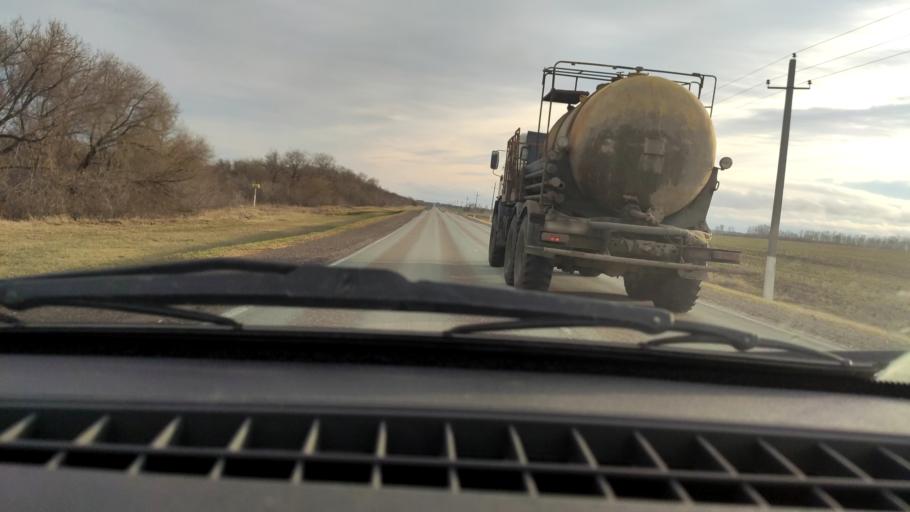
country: RU
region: Bashkortostan
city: Davlekanovo
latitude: 54.3164
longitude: 55.1506
